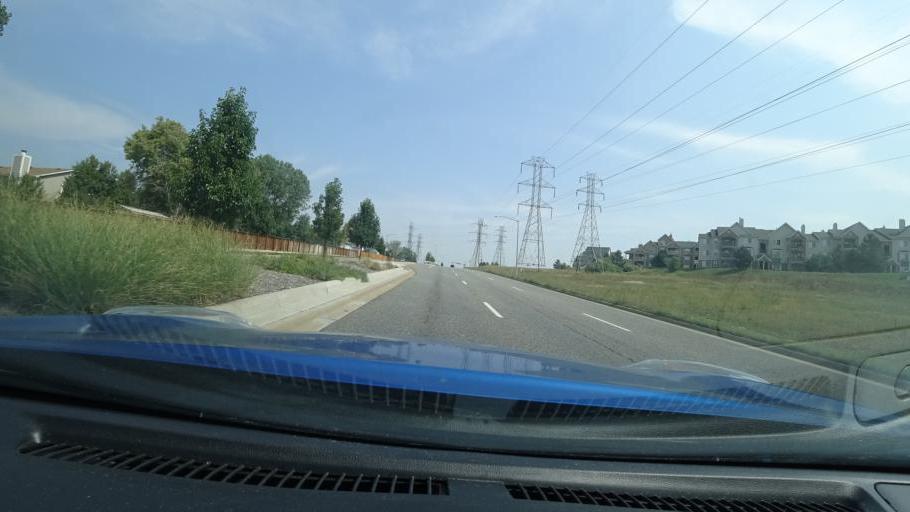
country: US
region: Colorado
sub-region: Adams County
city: Aurora
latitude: 39.6796
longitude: -104.7724
